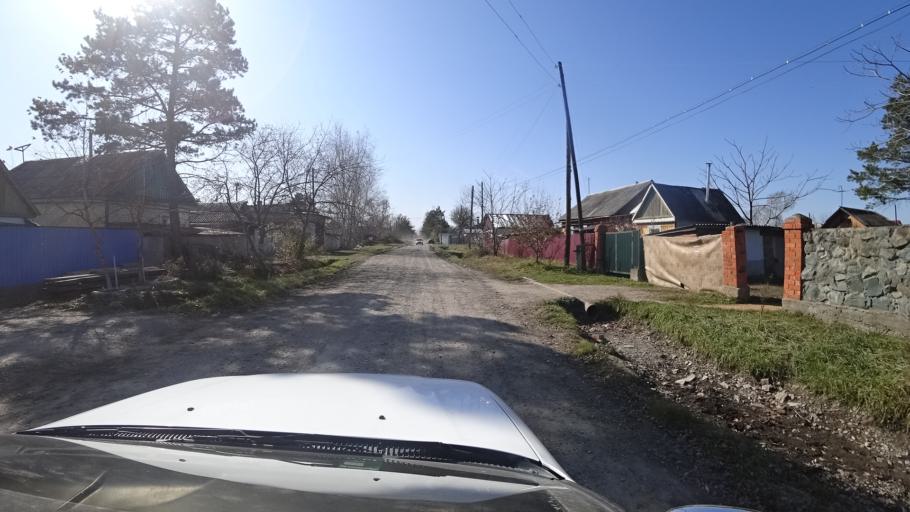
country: RU
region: Primorskiy
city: Dal'nerechensk
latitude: 45.9299
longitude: 133.7516
